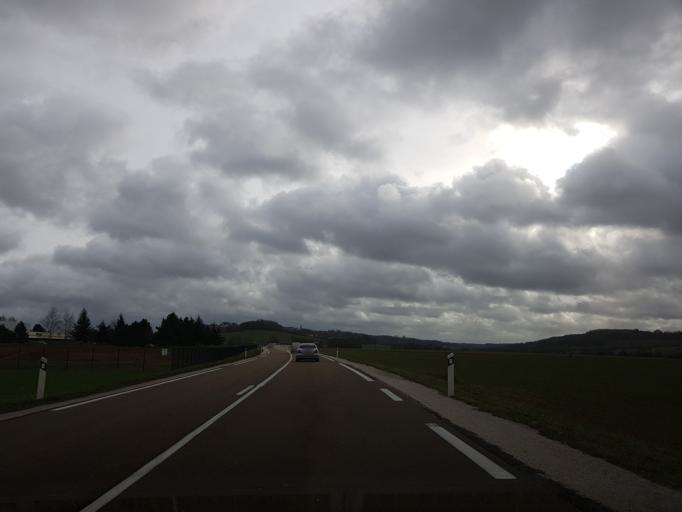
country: FR
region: Champagne-Ardenne
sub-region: Departement de la Haute-Marne
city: Langres
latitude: 47.8907
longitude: 5.3153
